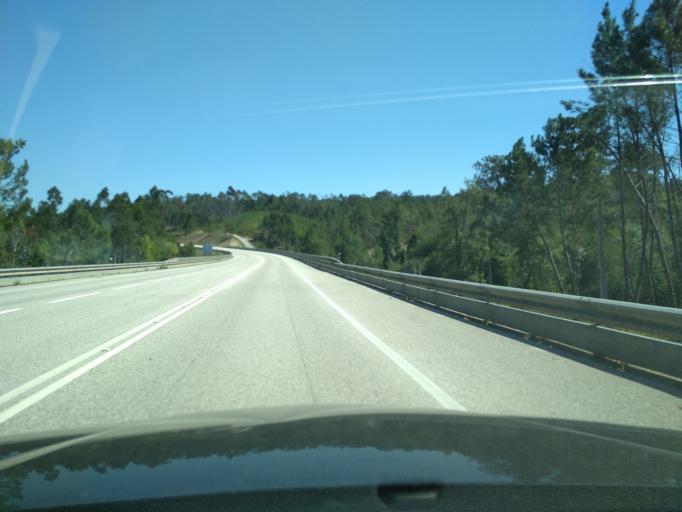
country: PT
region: Leiria
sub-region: Pombal
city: Lourical
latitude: 39.9867
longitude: -8.7668
